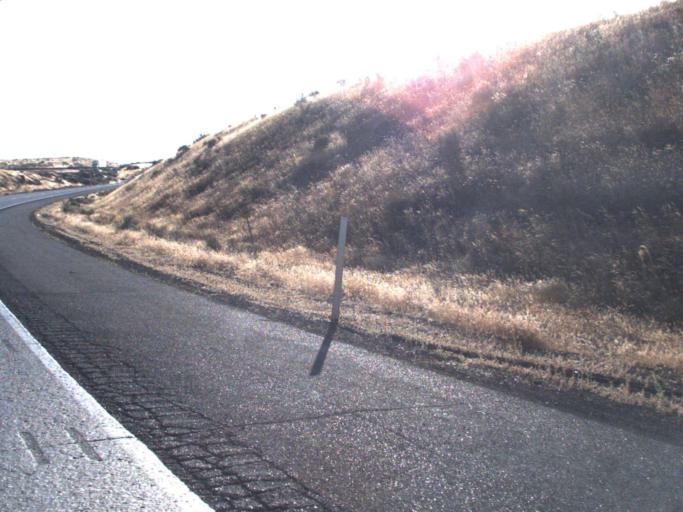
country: US
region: Washington
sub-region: Yakima County
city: Terrace Heights
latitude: 46.7122
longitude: -120.4276
